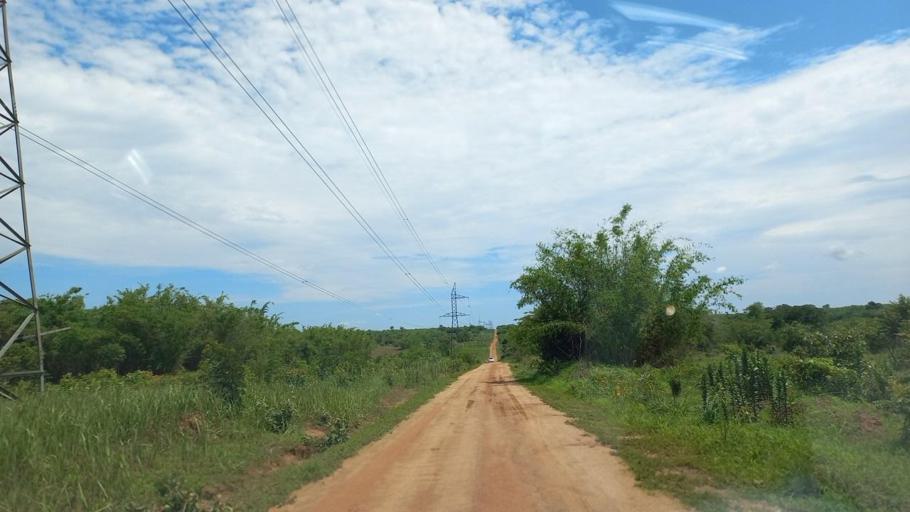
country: ZM
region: Copperbelt
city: Kitwe
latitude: -12.8157
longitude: 28.3566
